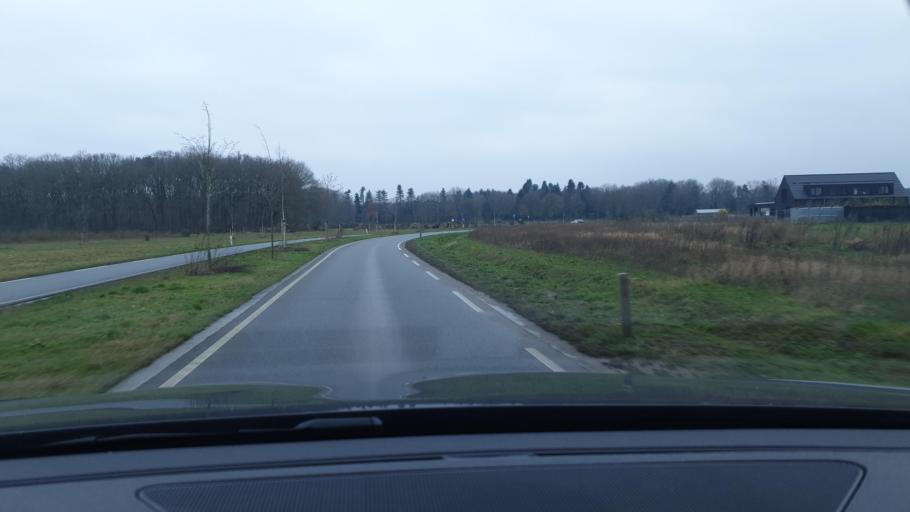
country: NL
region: North Brabant
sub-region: Gemeente Veldhoven
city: Oerle
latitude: 51.4077
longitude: 5.3712
